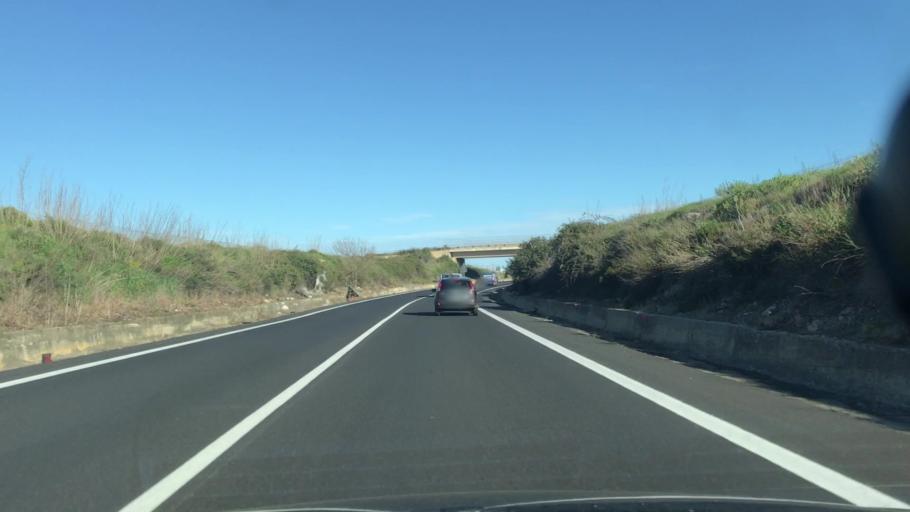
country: IT
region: Sicily
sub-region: Ragusa
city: Comiso
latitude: 36.9324
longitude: 14.6541
